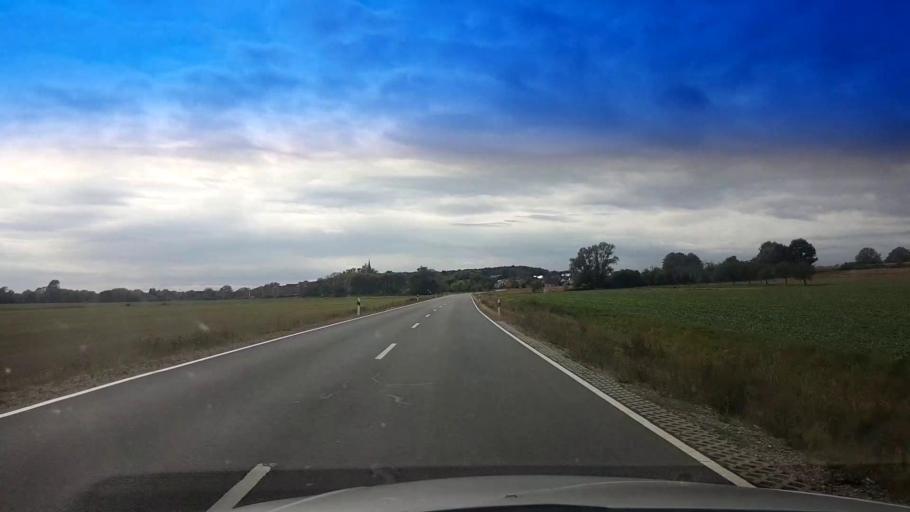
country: DE
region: Bavaria
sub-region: Upper Franconia
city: Frensdorf
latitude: 49.7944
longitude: 10.8981
